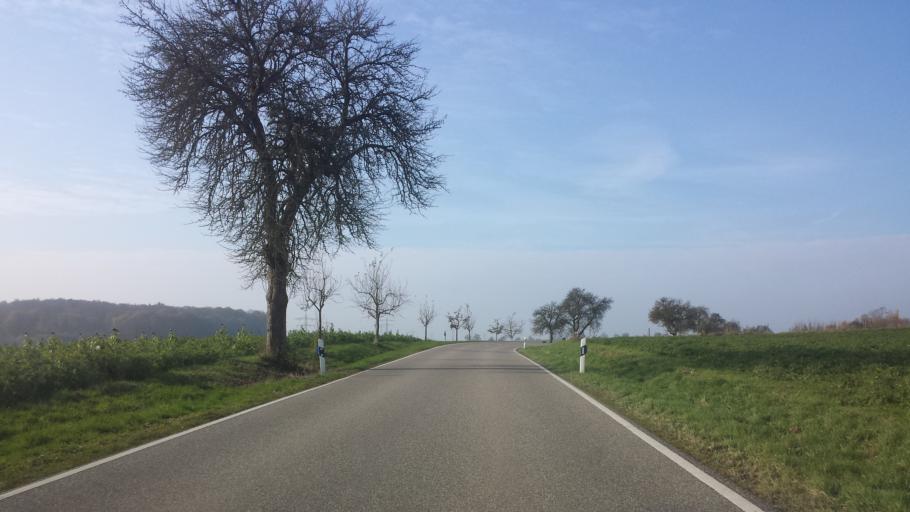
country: DE
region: Baden-Wuerttemberg
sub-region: Karlsruhe Region
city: Reichartshausen
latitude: 49.3292
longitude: 8.9466
